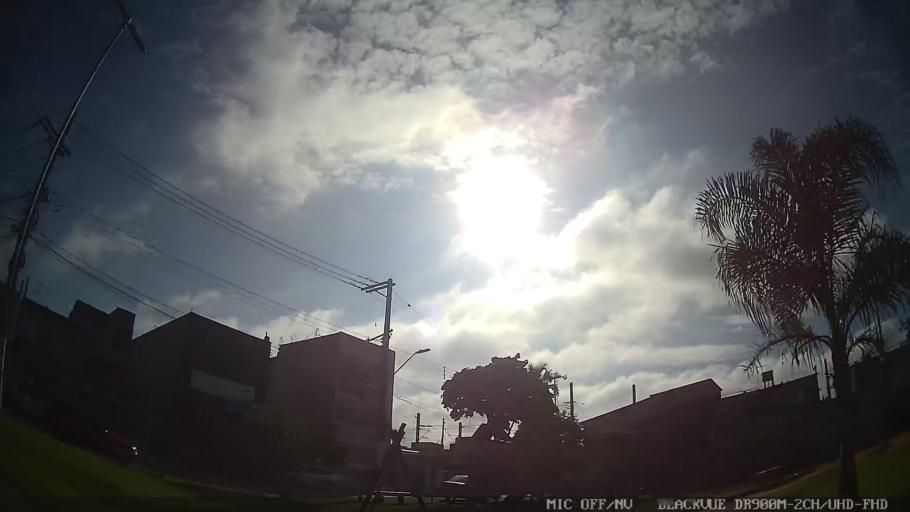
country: BR
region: Sao Paulo
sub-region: Itaquaquecetuba
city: Itaquaquecetuba
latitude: -23.4919
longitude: -46.3949
